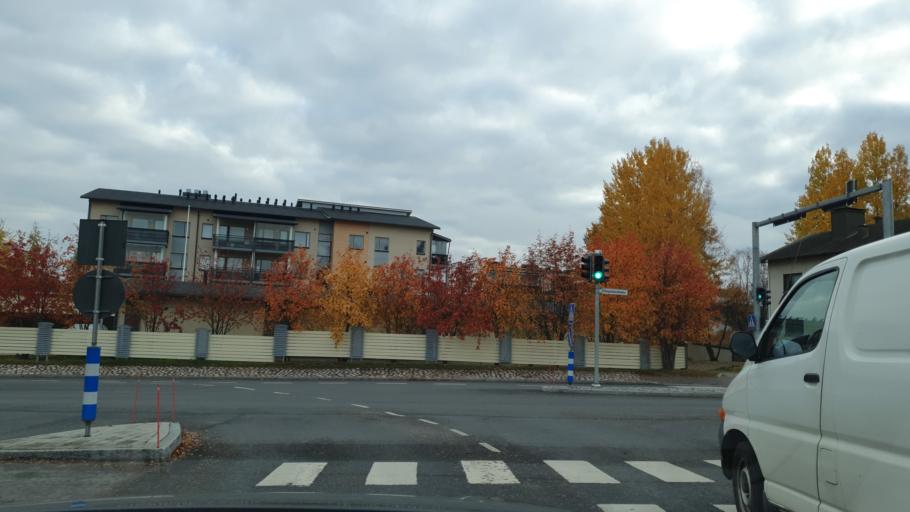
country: FI
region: Lapland
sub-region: Rovaniemi
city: Rovaniemi
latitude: 66.4951
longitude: 25.7297
